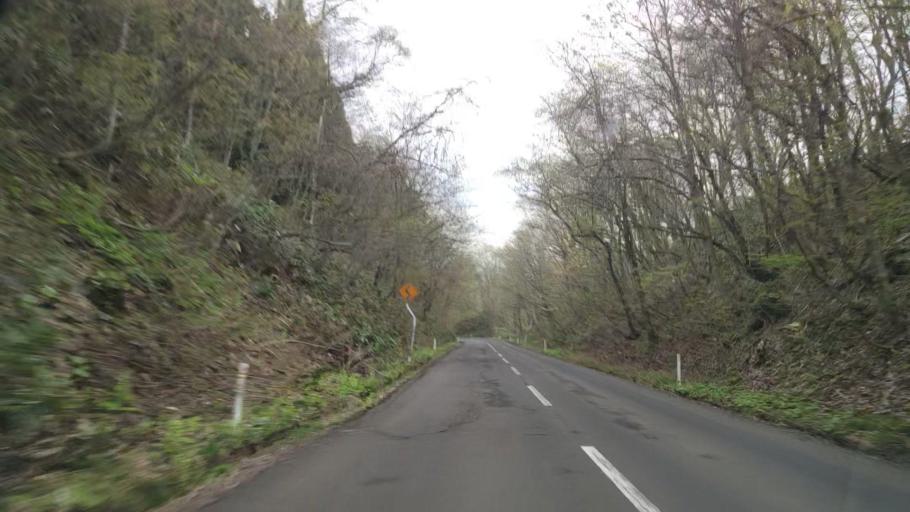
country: JP
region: Akita
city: Hanawa
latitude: 40.3831
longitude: 140.7917
